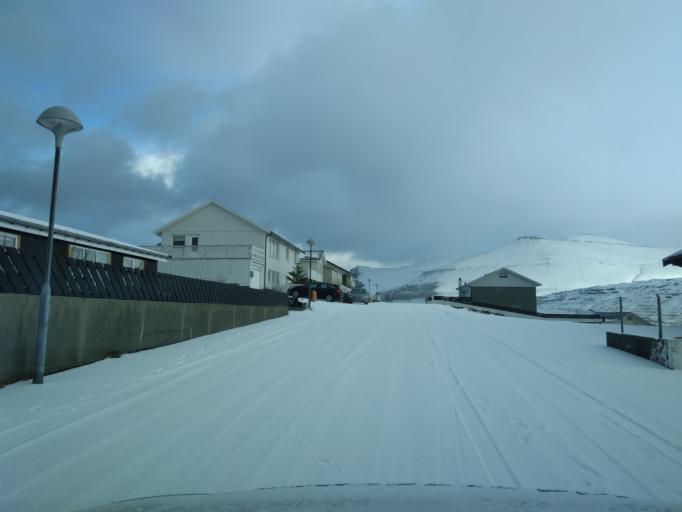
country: FO
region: Eysturoy
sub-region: Eidi
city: Eidi
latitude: 62.3016
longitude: -7.1003
